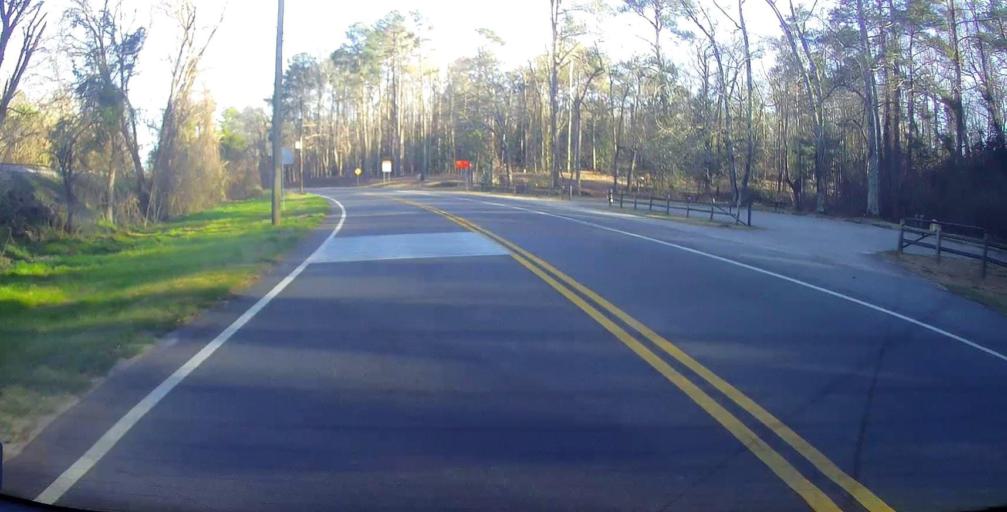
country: US
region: Georgia
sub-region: Meriwether County
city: Manchester
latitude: 32.8921
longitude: -84.6881
